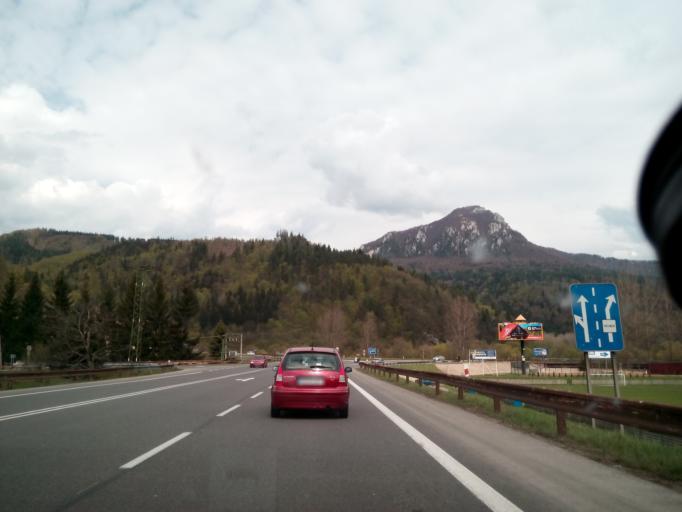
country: SK
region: Zilinsky
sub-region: Okres Zilina
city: Terchova
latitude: 49.1511
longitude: 19.1356
